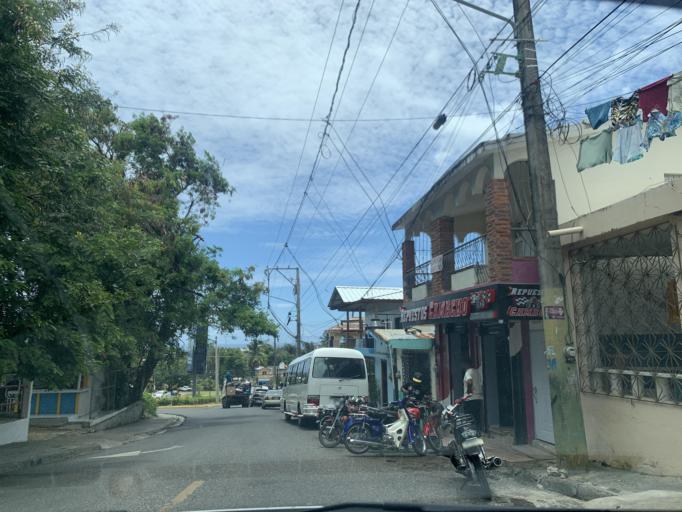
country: DO
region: Puerto Plata
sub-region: Puerto Plata
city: Puerto Plata
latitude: 19.7860
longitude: -70.6912
